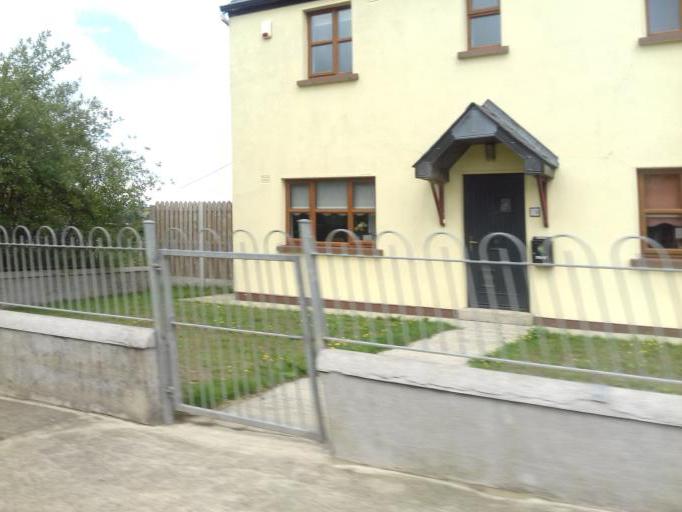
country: IE
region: Leinster
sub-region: Loch Garman
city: Ballinroad
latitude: 52.4779
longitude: -6.4156
